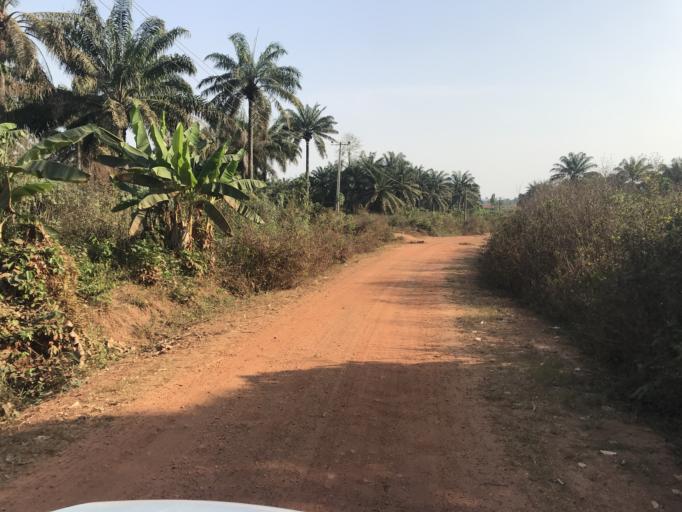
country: NG
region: Osun
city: Awo
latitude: 7.7585
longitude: 4.3165
